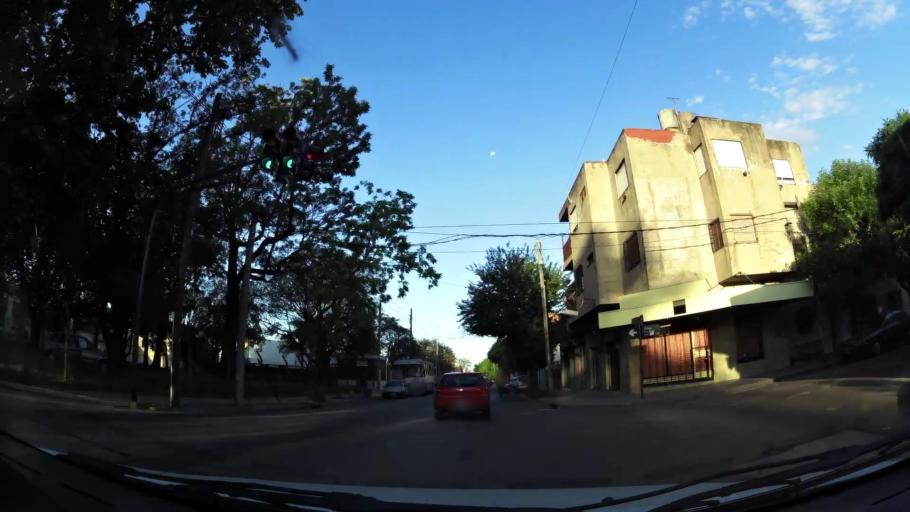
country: AR
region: Buenos Aires
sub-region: Partido de General San Martin
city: General San Martin
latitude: -34.5531
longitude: -58.5154
